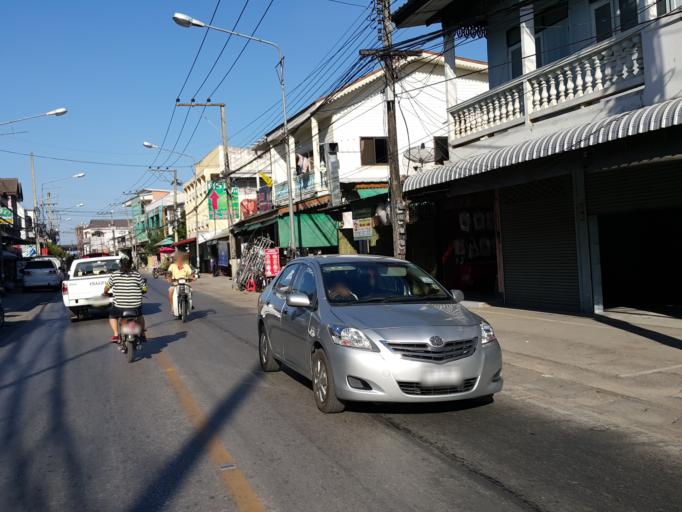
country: TH
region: Chiang Mai
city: San Kamphaeng
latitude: 18.7657
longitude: 99.0827
